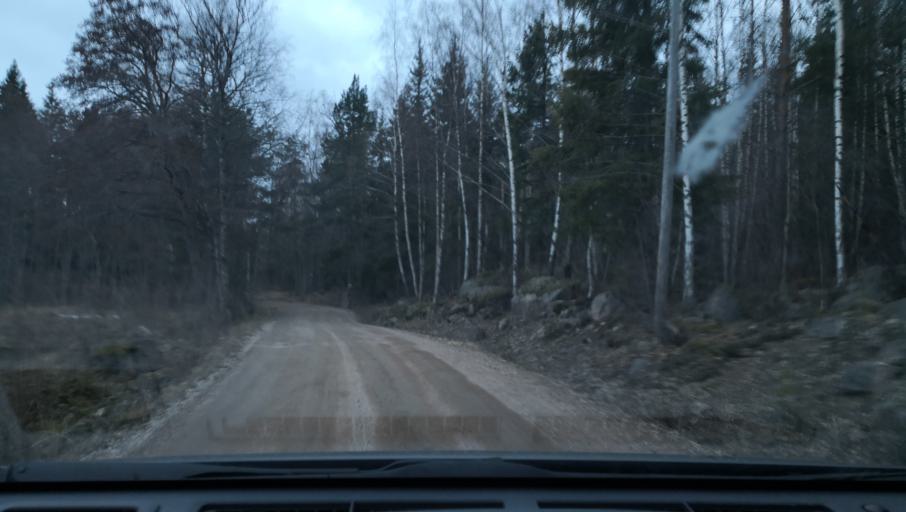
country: SE
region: OErebro
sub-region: Lindesbergs Kommun
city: Fellingsbro
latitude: 59.5768
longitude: 15.5666
